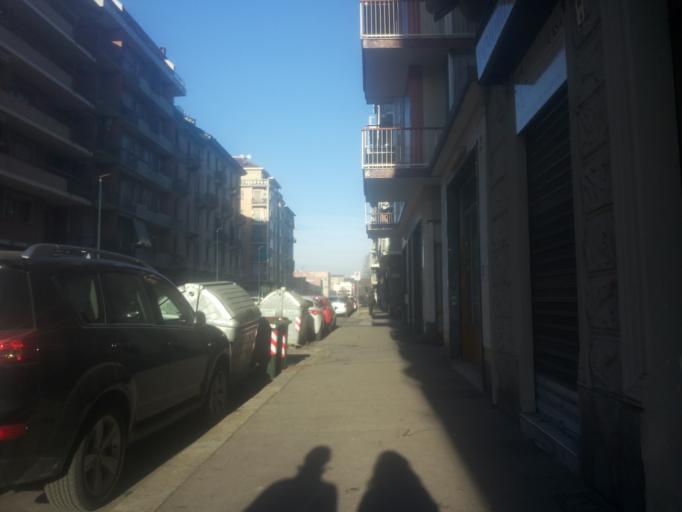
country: IT
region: Piedmont
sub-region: Provincia di Torino
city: Lesna
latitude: 45.0559
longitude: 7.6501
